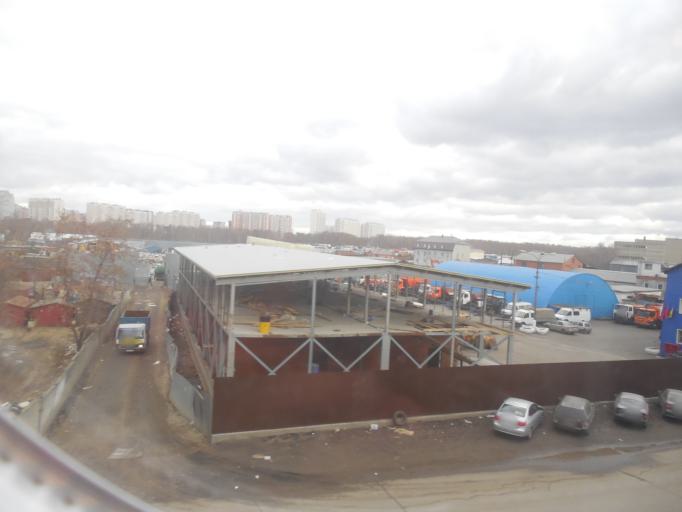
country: RU
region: Moskovskaya
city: Lyubertsy
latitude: 55.6787
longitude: 37.9045
